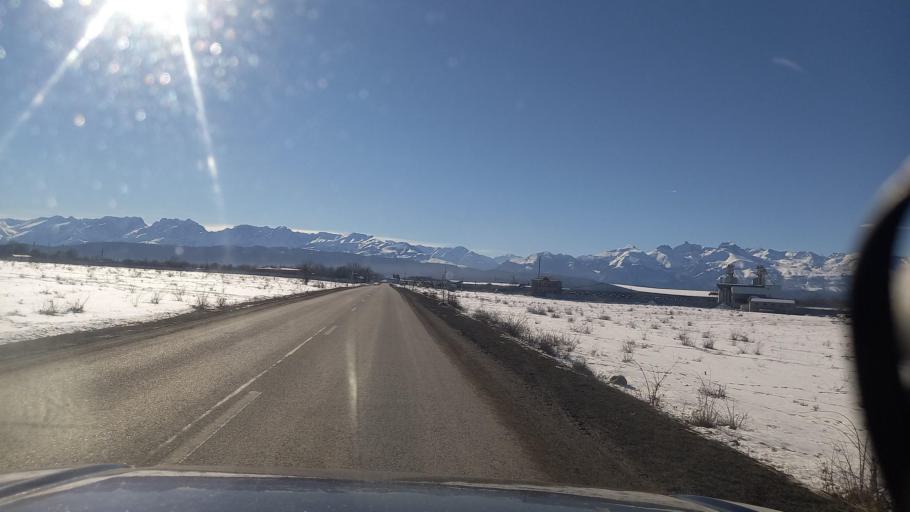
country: RU
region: North Ossetia
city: Chikola
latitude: 43.2124
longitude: 43.9220
